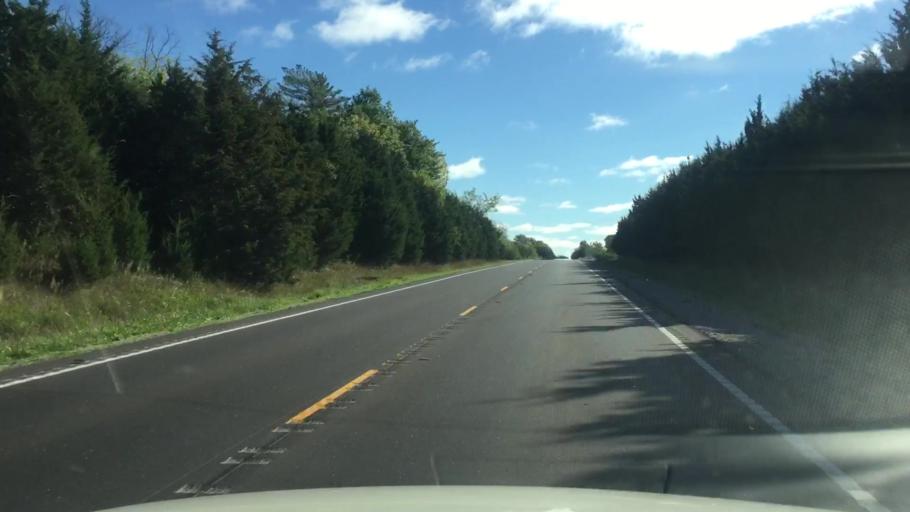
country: US
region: Missouri
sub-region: Boone County
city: Columbia
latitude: 38.9899
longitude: -92.5220
